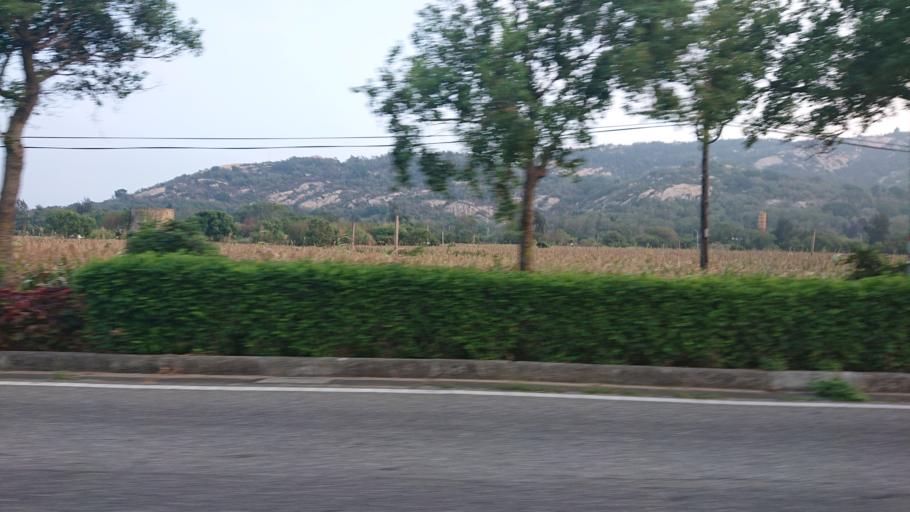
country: TW
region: Fukien
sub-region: Kinmen
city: Jincheng
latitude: 24.4775
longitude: 118.4208
